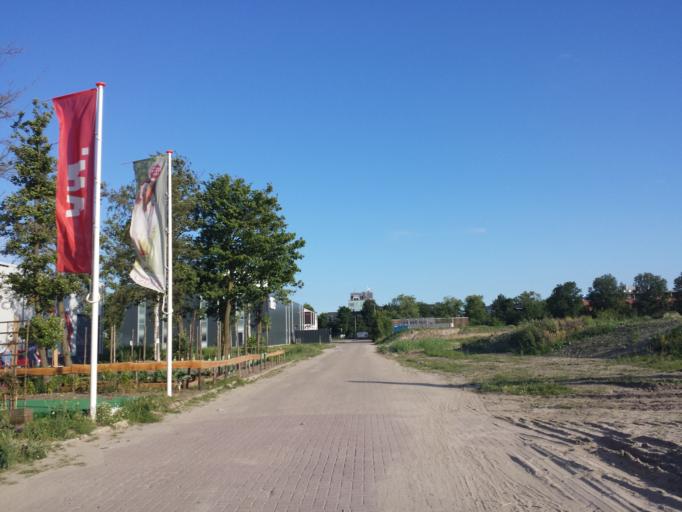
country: NL
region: South Holland
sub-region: Gemeente Delft
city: Delft
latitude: 52.0003
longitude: 4.3827
